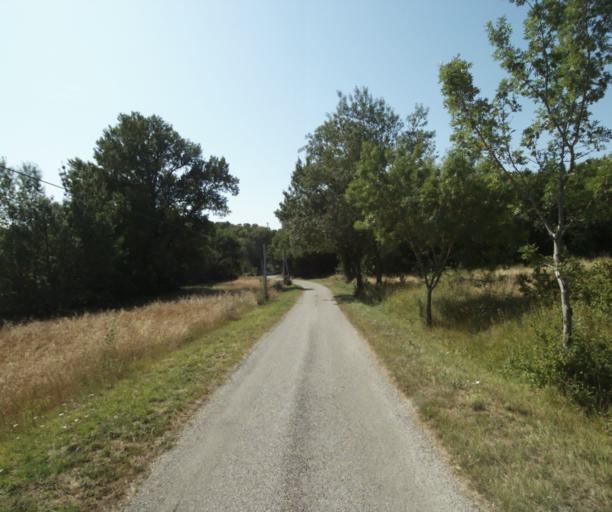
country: FR
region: Midi-Pyrenees
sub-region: Departement de la Haute-Garonne
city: Saint-Felix-Lauragais
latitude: 43.4559
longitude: 1.8430
